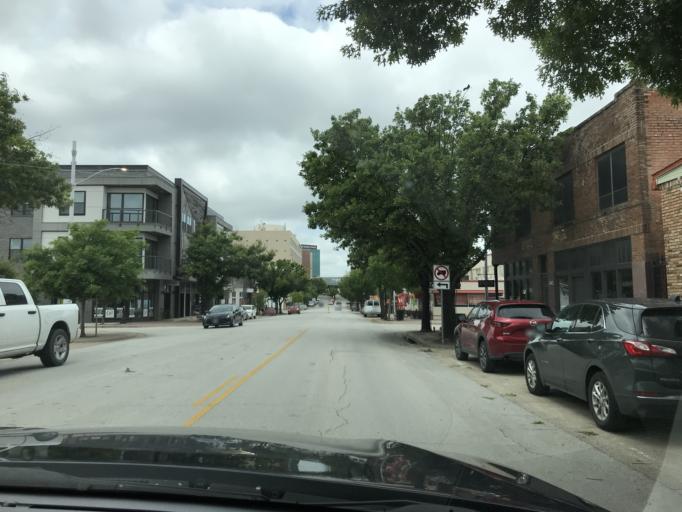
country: US
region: Texas
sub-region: Tarrant County
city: Fort Worth
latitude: 32.7307
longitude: -97.3406
